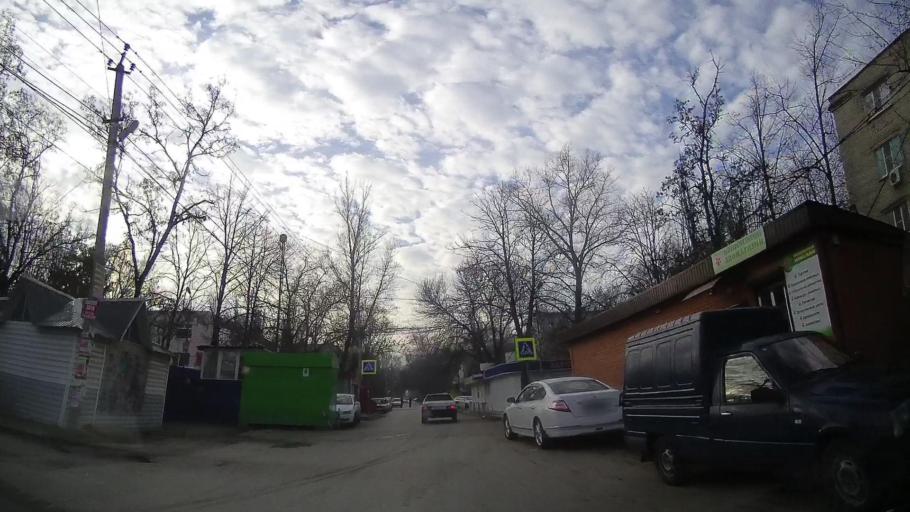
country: RU
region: Rostov
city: Bataysk
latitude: 47.1268
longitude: 39.7787
